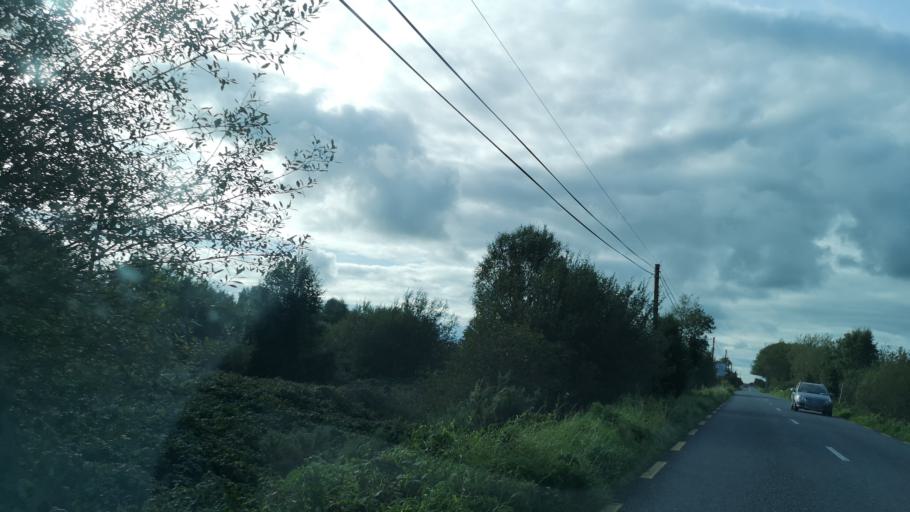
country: IE
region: Leinster
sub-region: Uibh Fhaili
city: Banagher
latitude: 53.2862
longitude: -8.0796
